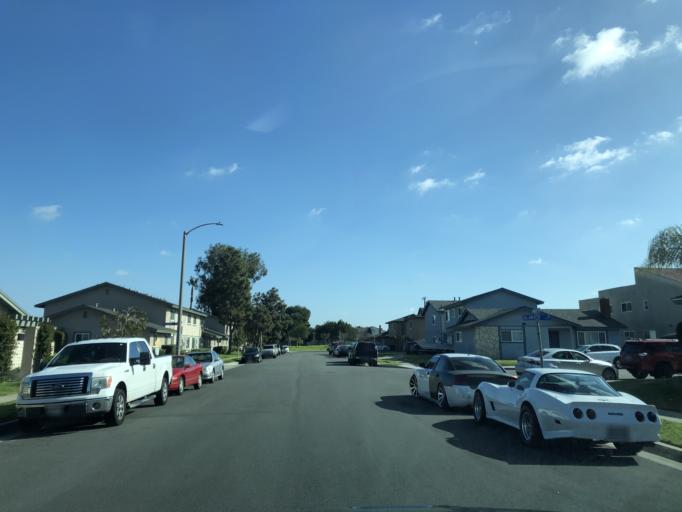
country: US
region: California
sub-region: Orange County
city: Westminster
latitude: 33.7207
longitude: -118.0472
